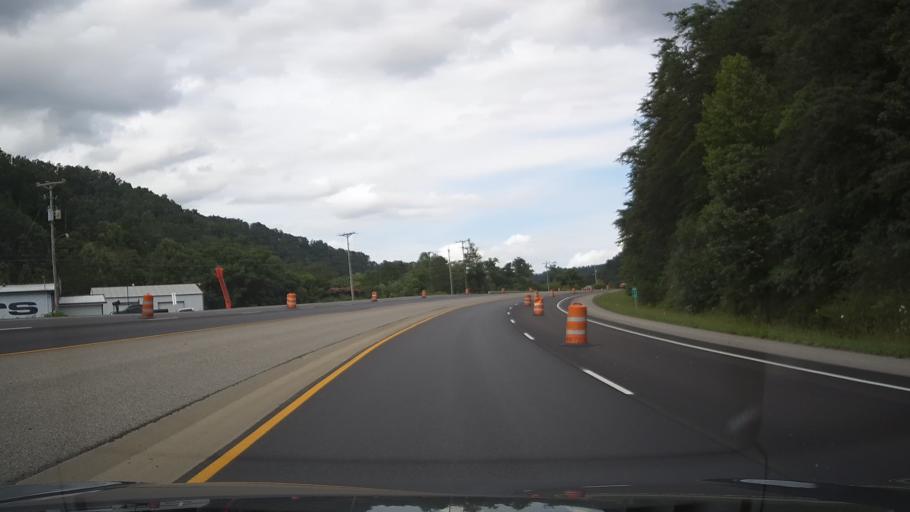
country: US
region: Kentucky
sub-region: Pike County
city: Pikeville
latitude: 37.3635
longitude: -82.5543
